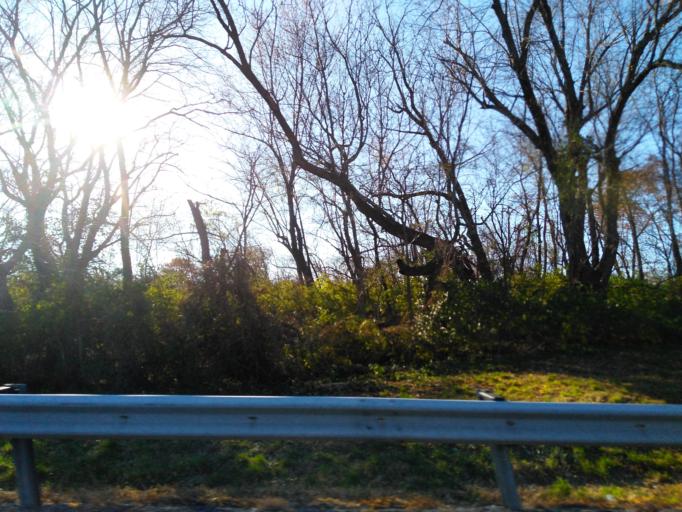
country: US
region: Illinois
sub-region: Madison County
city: Maryville
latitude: 38.7061
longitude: -89.9691
